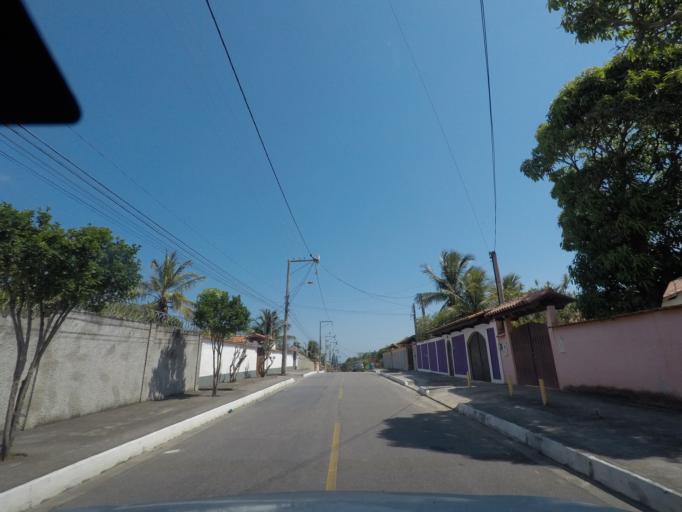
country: BR
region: Rio de Janeiro
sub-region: Marica
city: Marica
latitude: -22.9654
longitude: -42.9649
